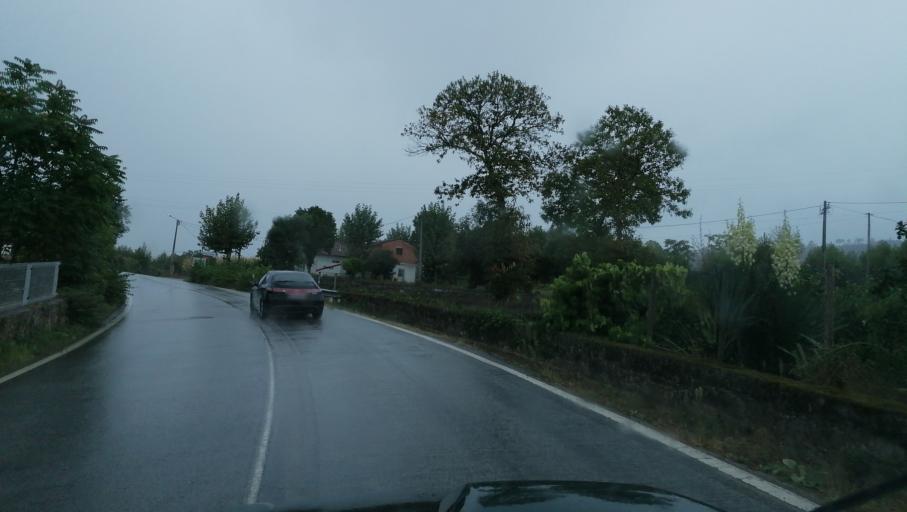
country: PT
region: Braga
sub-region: Cabeceiras de Basto
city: Cabeceiras de Basto
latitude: 41.4985
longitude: -7.9159
